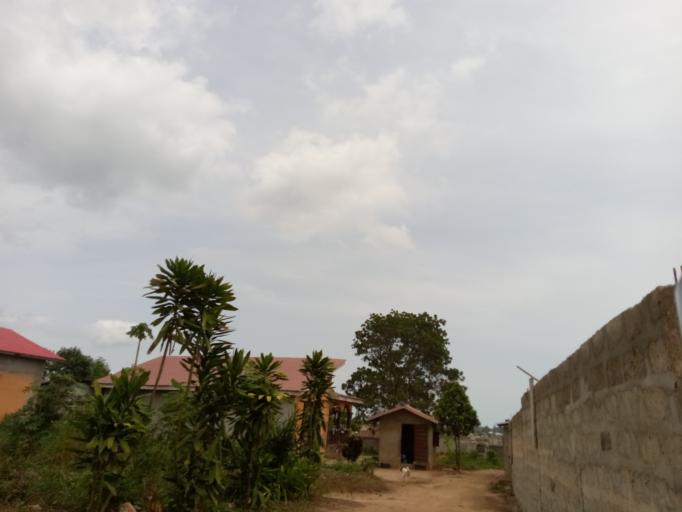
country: SL
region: Western Area
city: Waterloo
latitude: 8.3325
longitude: -13.0241
